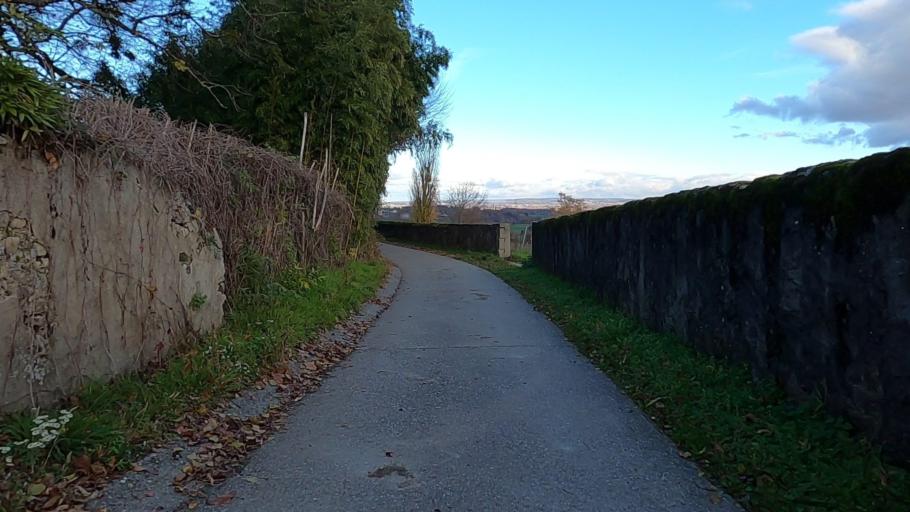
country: CH
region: Vaud
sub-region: Morges District
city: Saint-Prex
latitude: 46.5169
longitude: 6.4601
